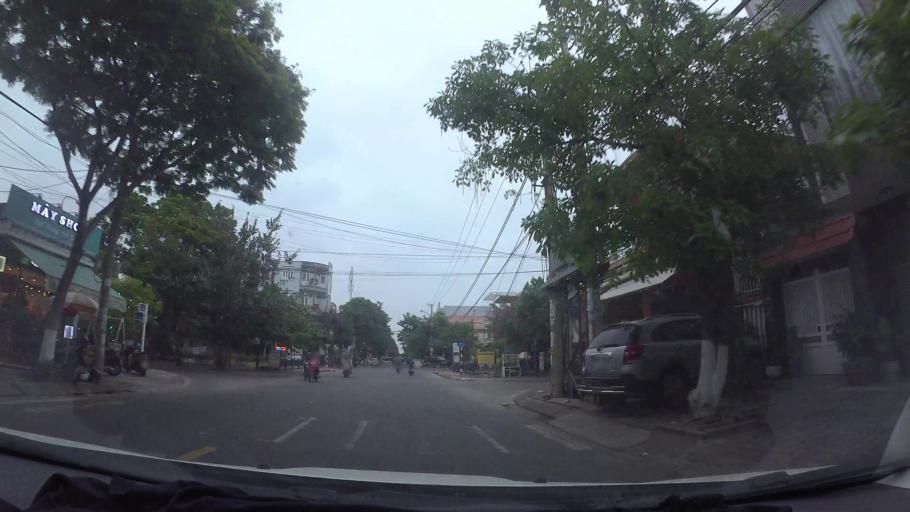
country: VN
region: Da Nang
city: Lien Chieu
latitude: 16.0784
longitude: 108.1608
